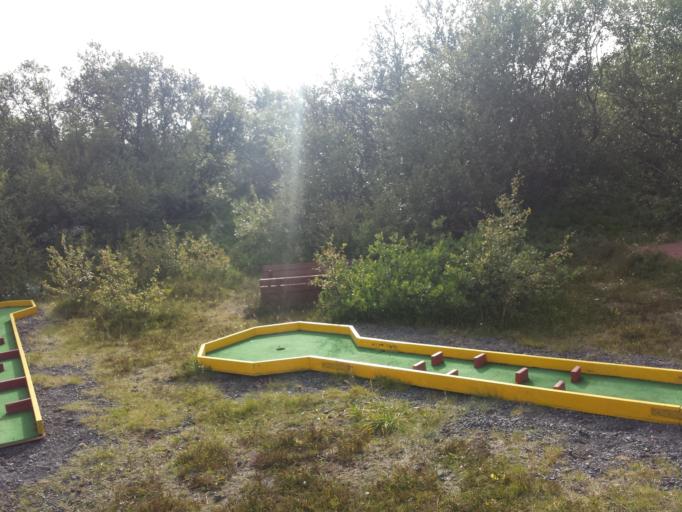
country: IS
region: Northeast
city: Husavik
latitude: 65.9460
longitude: -17.4212
